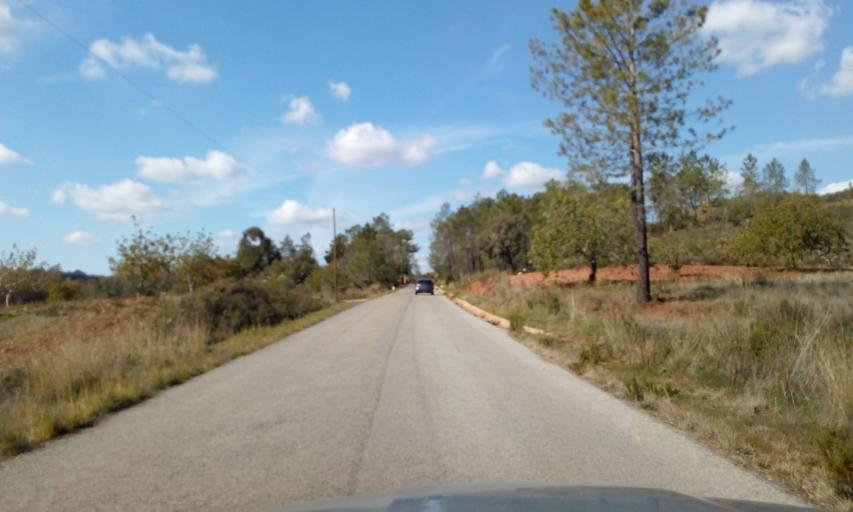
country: PT
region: Faro
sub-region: Loule
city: Loule
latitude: 37.2458
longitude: -8.0718
